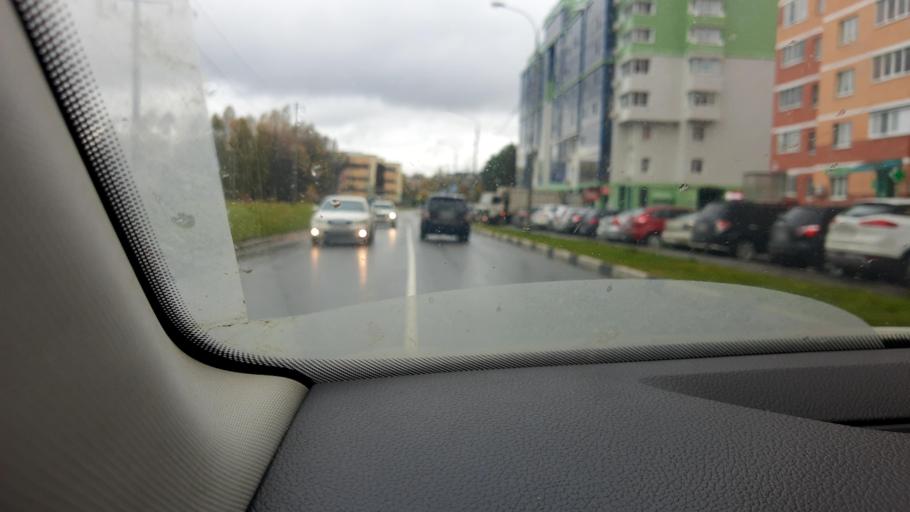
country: RU
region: Moskovskaya
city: Aprelevka
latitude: 55.5453
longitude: 37.0847
